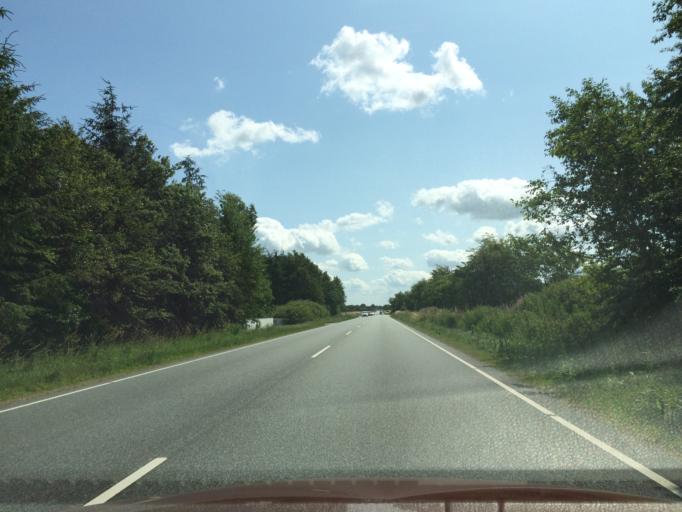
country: DK
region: Central Jutland
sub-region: Favrskov Kommune
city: Hammel
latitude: 56.2628
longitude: 9.7449
